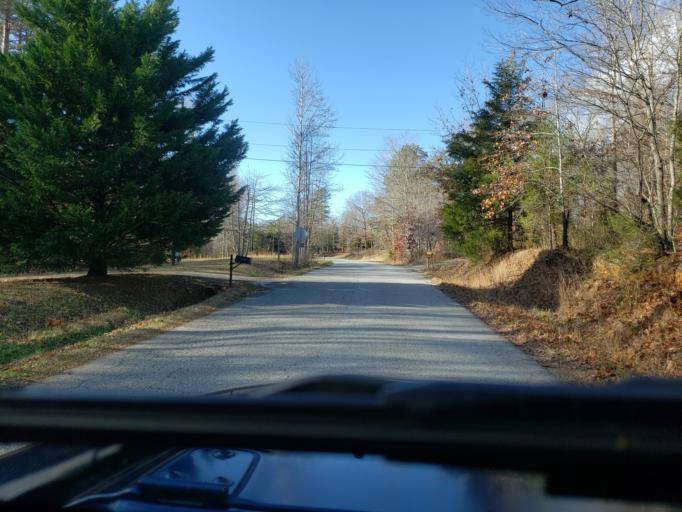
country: US
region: North Carolina
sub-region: Cleveland County
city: Kings Mountain
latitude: 35.1601
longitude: -81.3411
